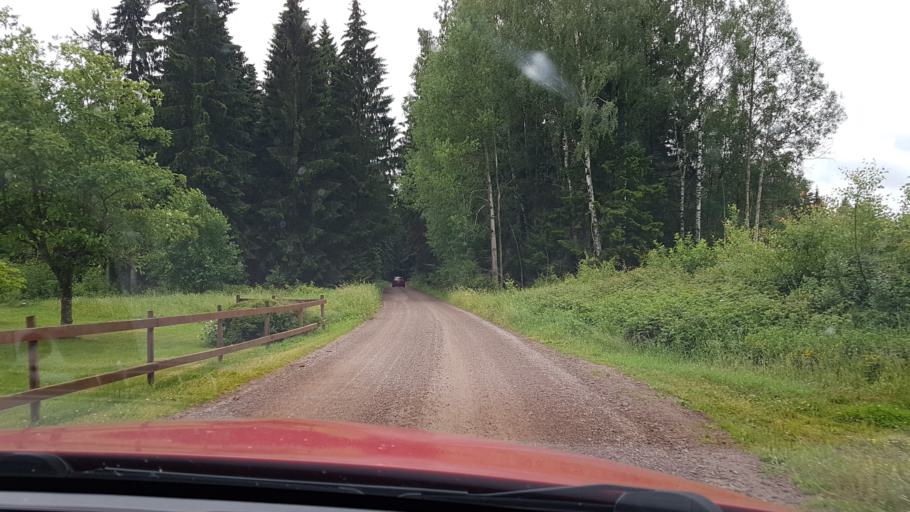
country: SE
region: Vaestra Goetaland
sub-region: Tibro Kommun
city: Tibro
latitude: 58.4289
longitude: 14.1253
